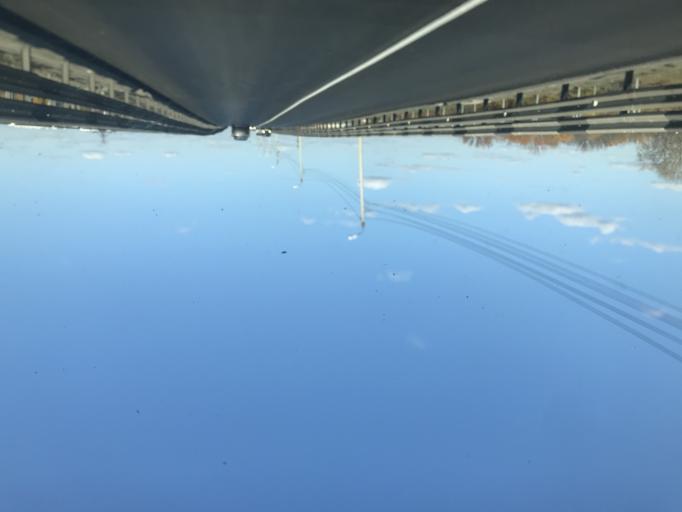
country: RU
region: Chelyabinsk
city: Roshchino
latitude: 55.2320
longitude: 61.2900
